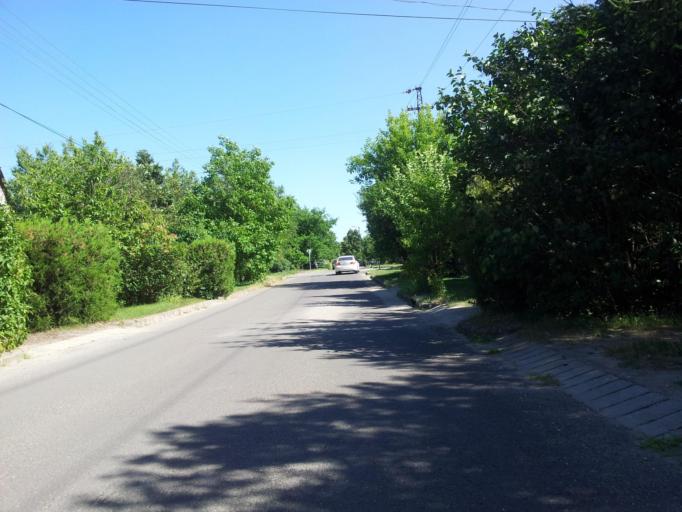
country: HU
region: Pest
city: Veresegyhaz
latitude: 47.6468
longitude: 19.2716
